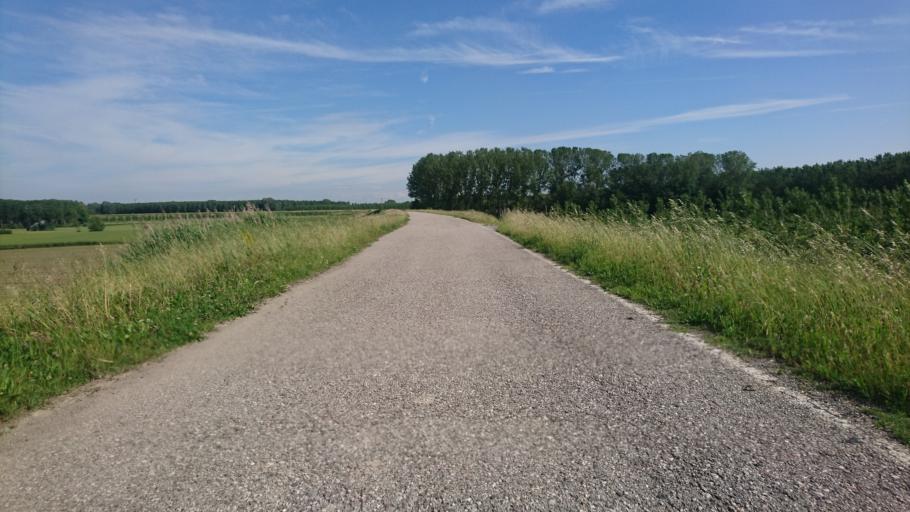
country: IT
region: Veneto
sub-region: Provincia di Rovigo
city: Bergantino
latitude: 45.0442
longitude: 11.2633
